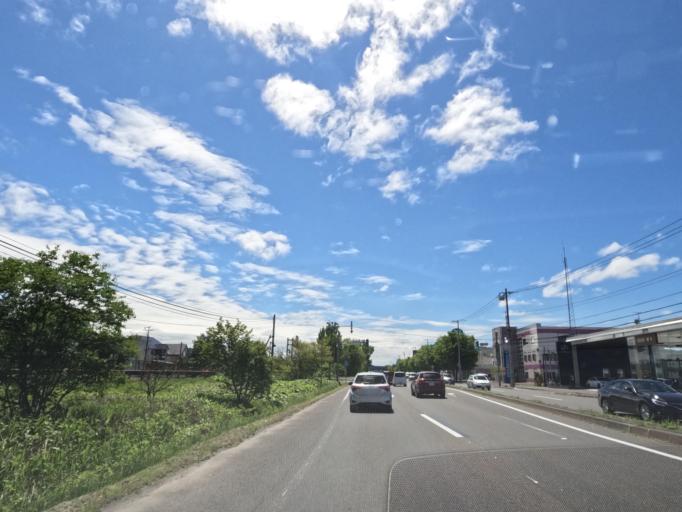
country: JP
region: Hokkaido
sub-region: Asahikawa-shi
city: Asahikawa
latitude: 43.7312
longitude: 142.3653
